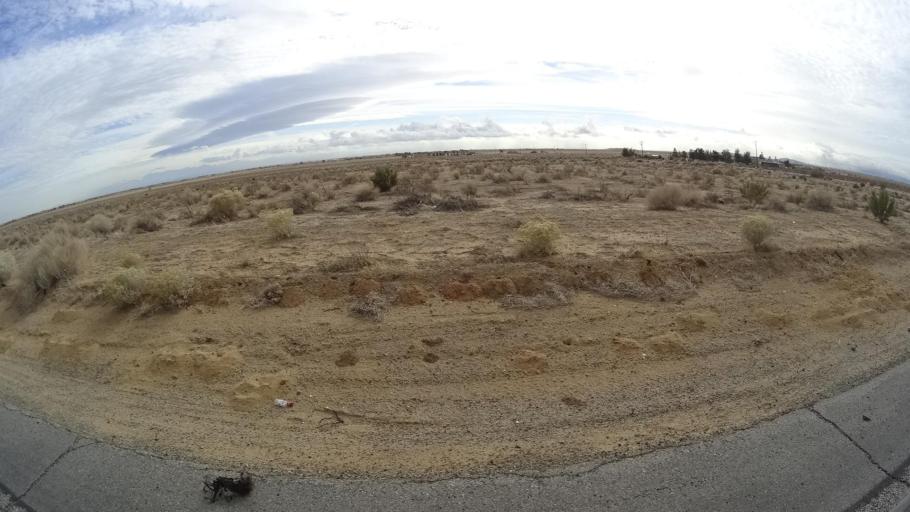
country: US
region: California
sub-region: Kern County
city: Rosamond
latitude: 34.8635
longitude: -118.2724
